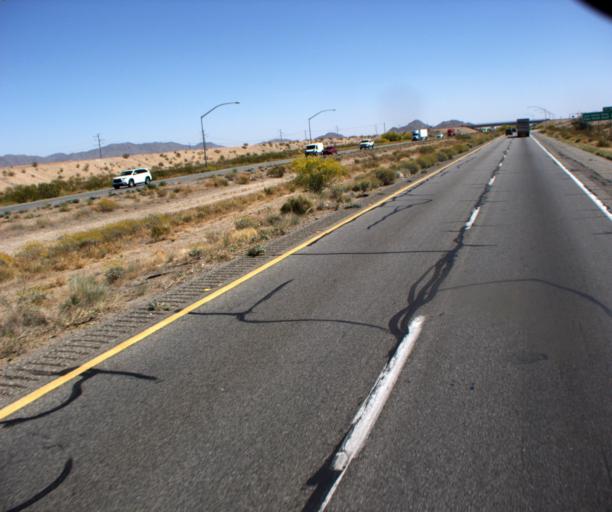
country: US
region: Arizona
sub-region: Maricopa County
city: Buckeye
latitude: 33.4409
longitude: -112.6854
